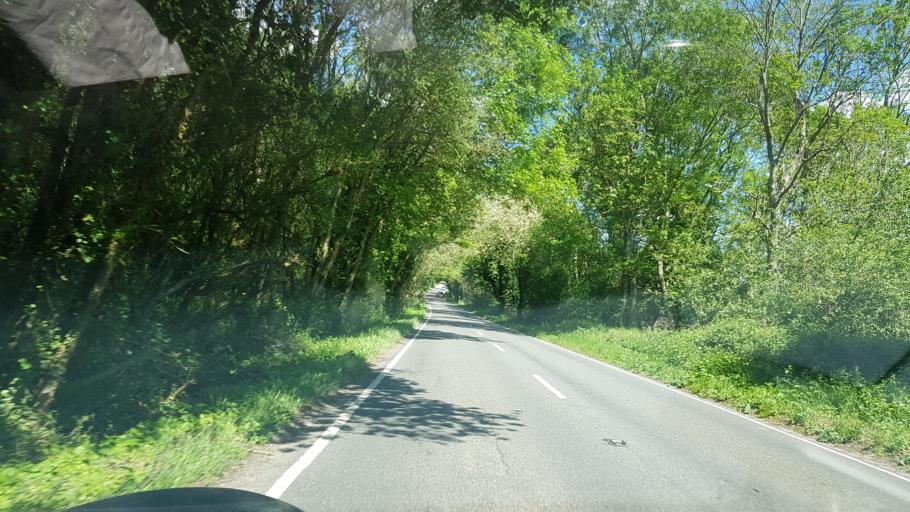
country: GB
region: England
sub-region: Surrey
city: Cranleigh
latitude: 51.1322
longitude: -0.5441
